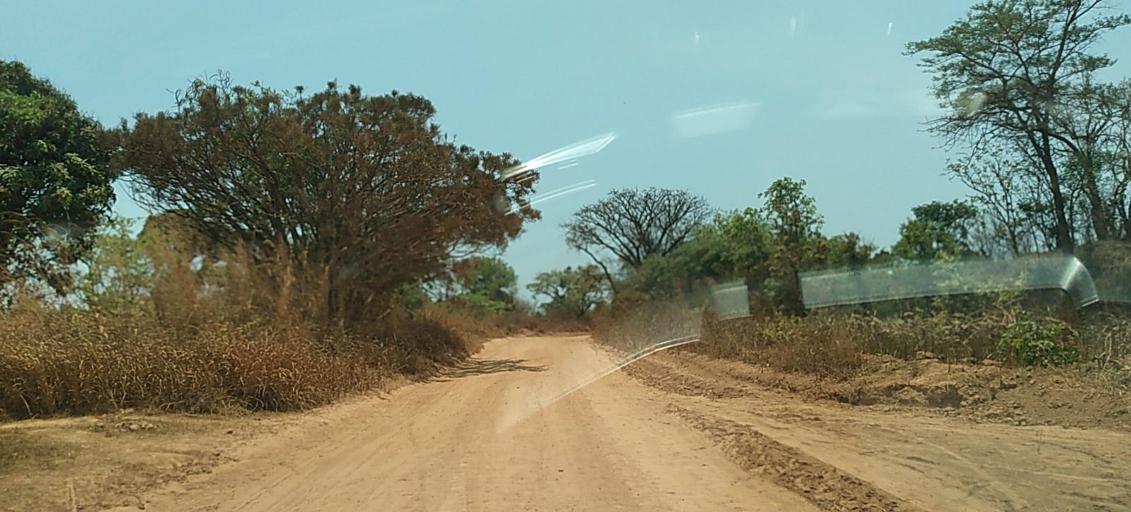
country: CD
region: Katanga
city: Kipushi
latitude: -11.7868
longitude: 27.1700
